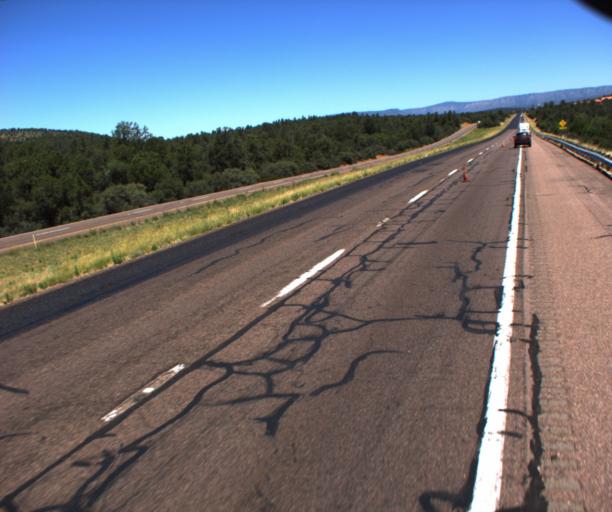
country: US
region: Arizona
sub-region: Gila County
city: Payson
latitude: 34.2065
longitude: -111.3312
